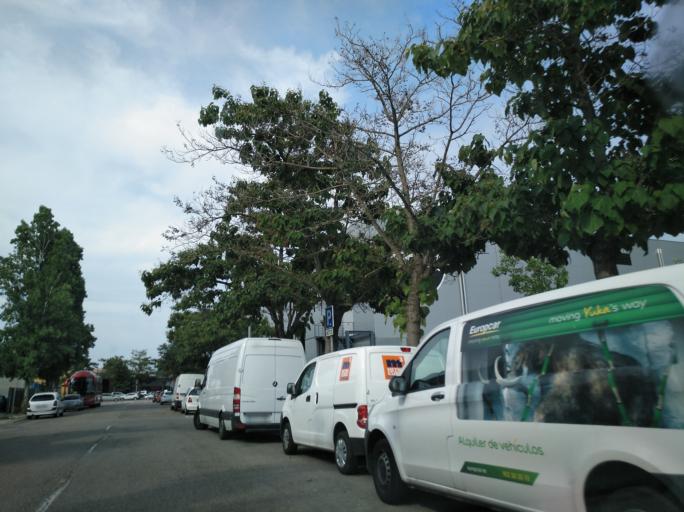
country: ES
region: Catalonia
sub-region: Provincia de Girona
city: Salt
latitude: 41.9652
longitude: 2.8059
